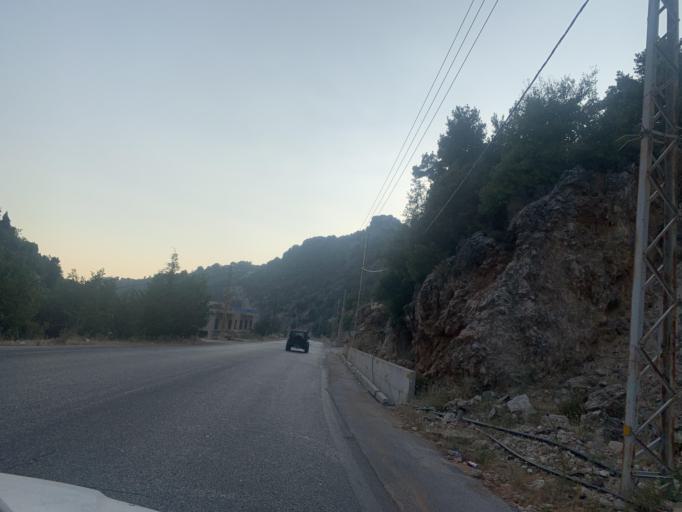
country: LB
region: Liban-Nord
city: Amioun
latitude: 34.1333
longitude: 35.8198
